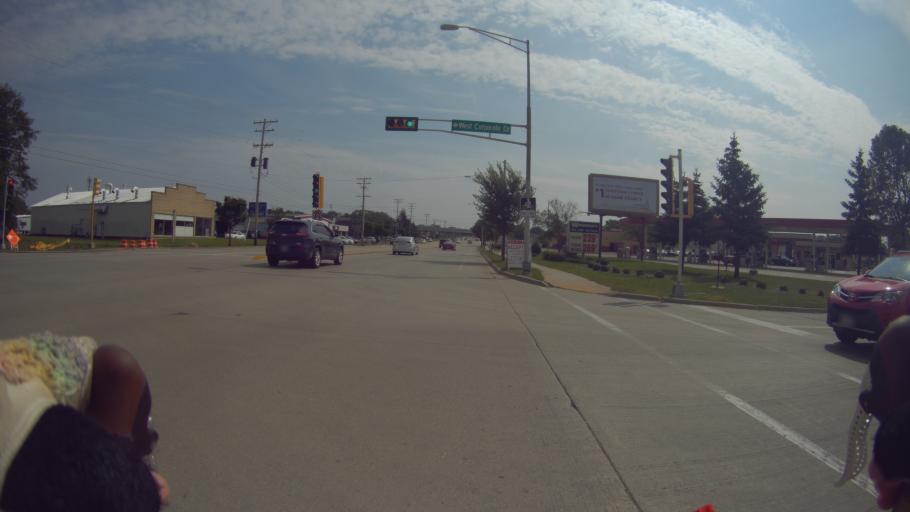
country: US
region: Wisconsin
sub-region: Dane County
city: Monona
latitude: 43.0983
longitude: -89.3219
